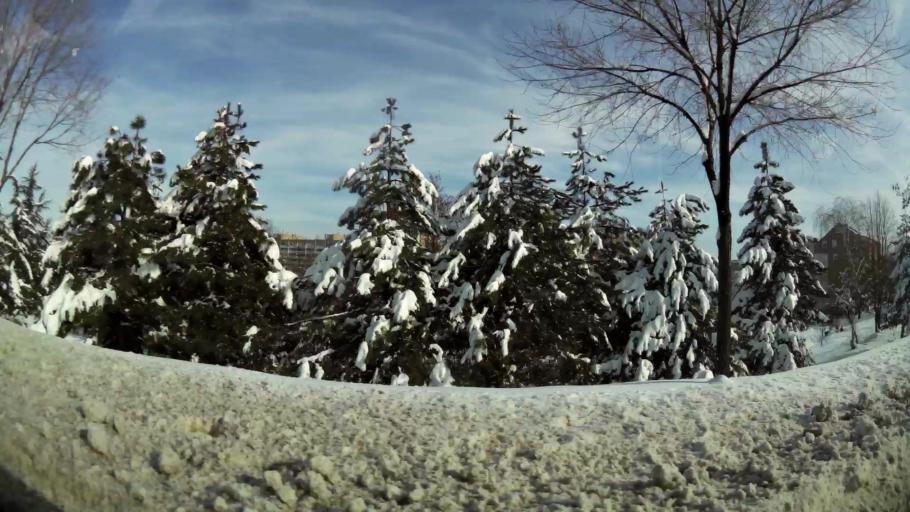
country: RS
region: Central Serbia
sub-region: Belgrade
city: Zvezdara
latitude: 44.7870
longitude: 20.5278
